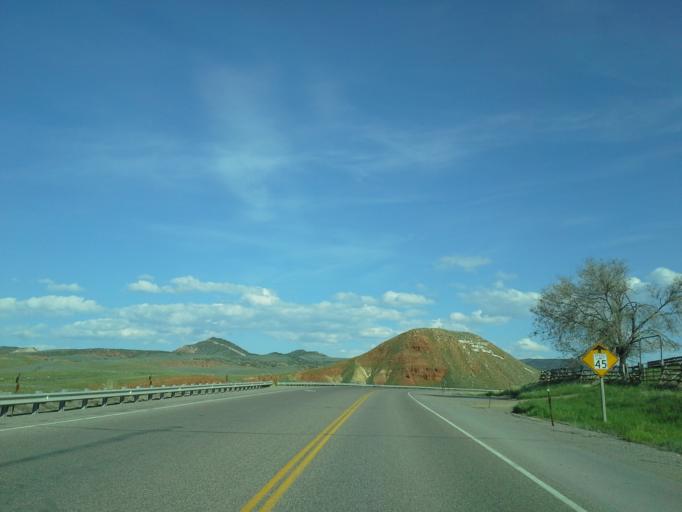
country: US
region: Wyoming
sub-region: Hot Springs County
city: Thermopolis
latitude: 43.6620
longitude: -108.1997
